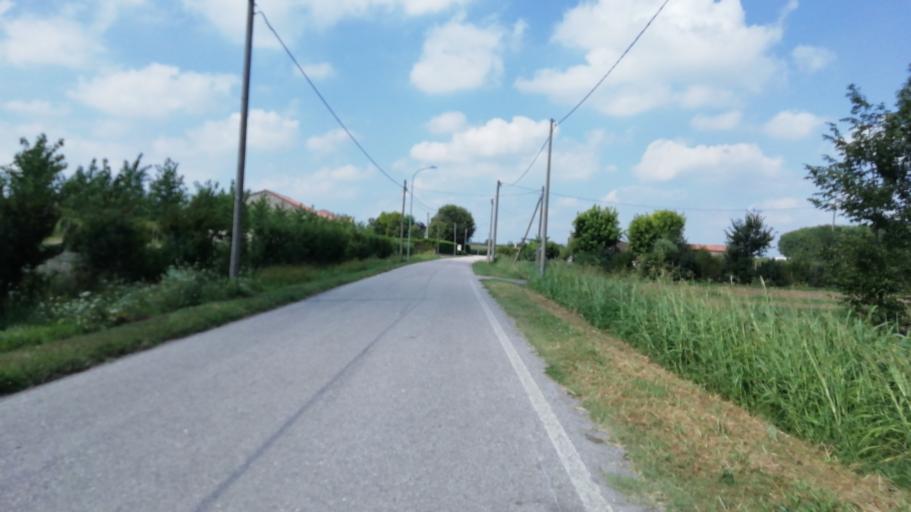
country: IT
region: Veneto
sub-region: Provincia di Rovigo
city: Gaiba
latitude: 44.9455
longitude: 11.4979
